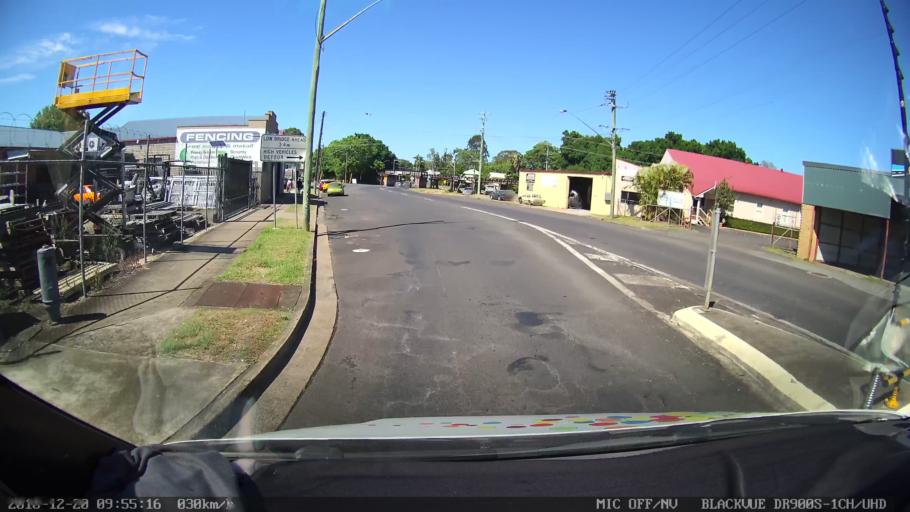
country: AU
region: New South Wales
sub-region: Lismore Municipality
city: Lismore
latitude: -28.8058
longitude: 153.2743
